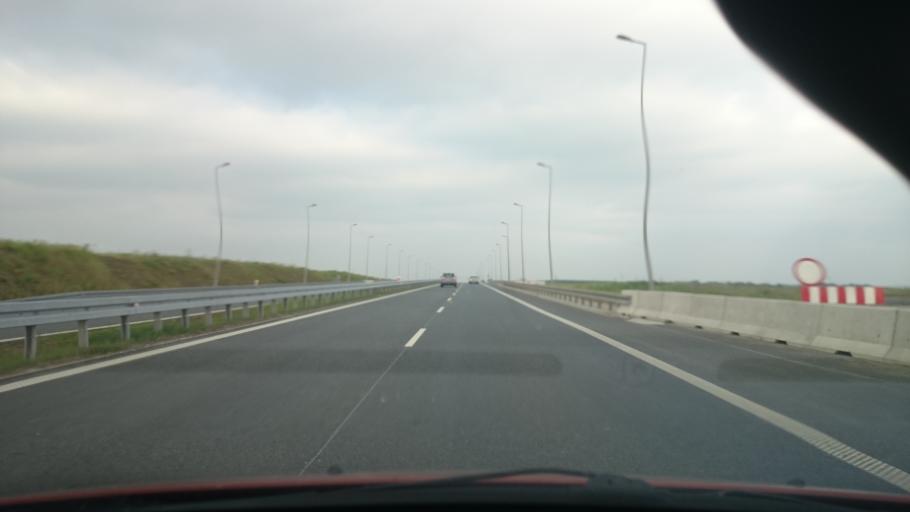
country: PL
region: Opole Voivodeship
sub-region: Powiat nyski
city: Nysa
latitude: 50.5014
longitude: 17.3324
